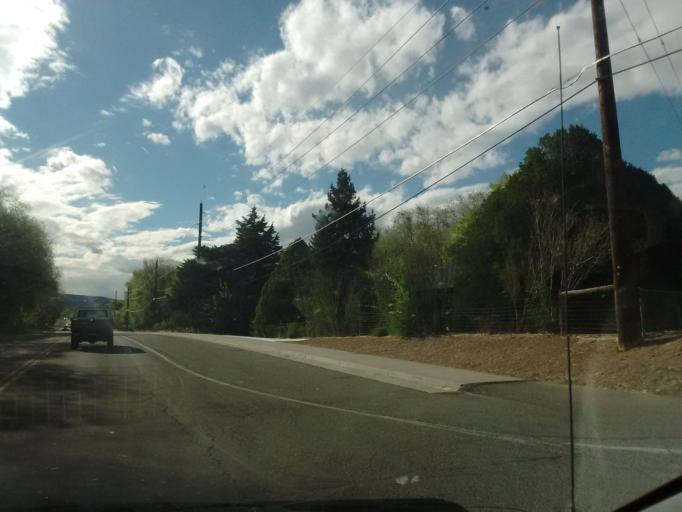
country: US
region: Colorado
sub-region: Mesa County
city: Redlands
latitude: 39.0678
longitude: -108.6052
